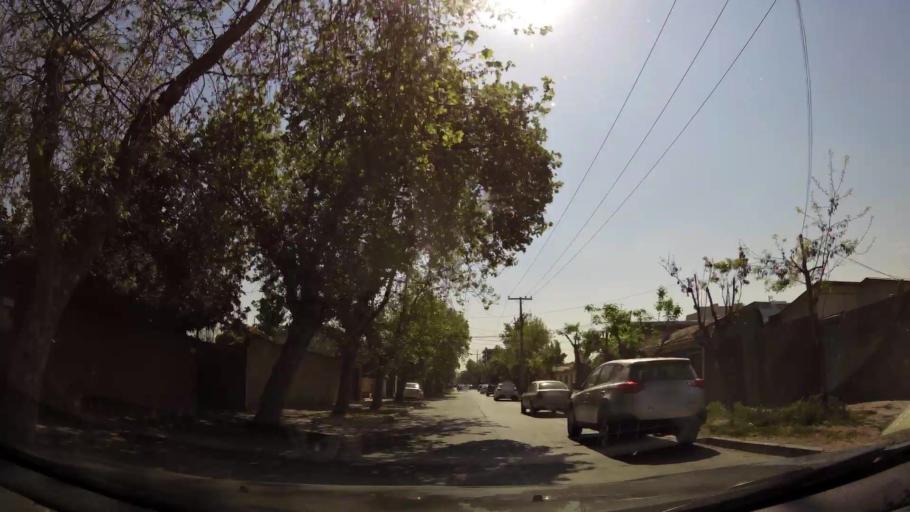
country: CL
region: Santiago Metropolitan
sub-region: Provincia de Maipo
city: San Bernardo
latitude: -33.5967
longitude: -70.7099
